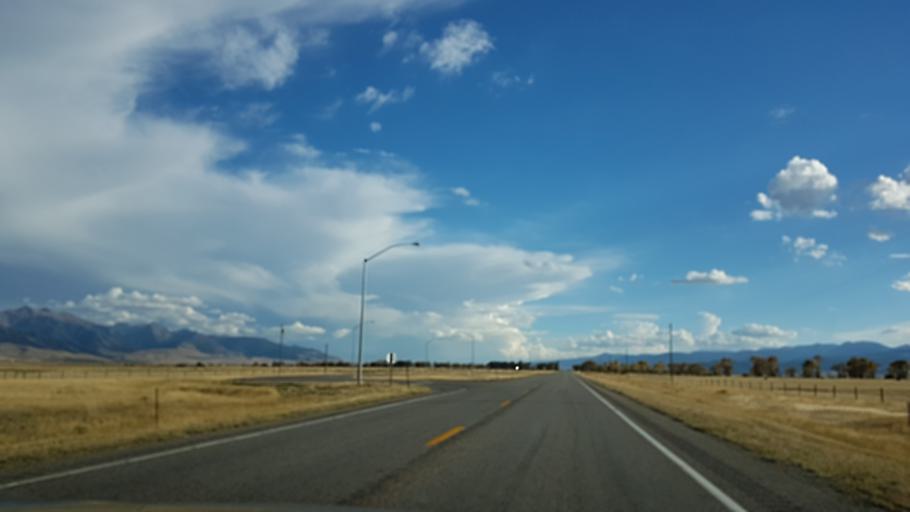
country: US
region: Montana
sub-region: Madison County
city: Virginia City
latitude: 45.2152
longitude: -111.6789
